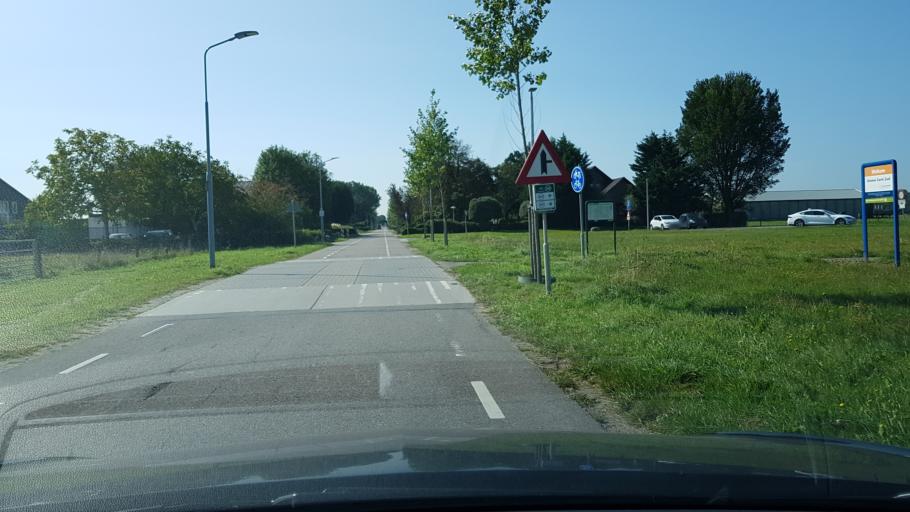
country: NL
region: North Holland
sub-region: Gemeente Haarlemmermeer
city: Hoofddorp
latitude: 52.3009
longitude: 4.7260
